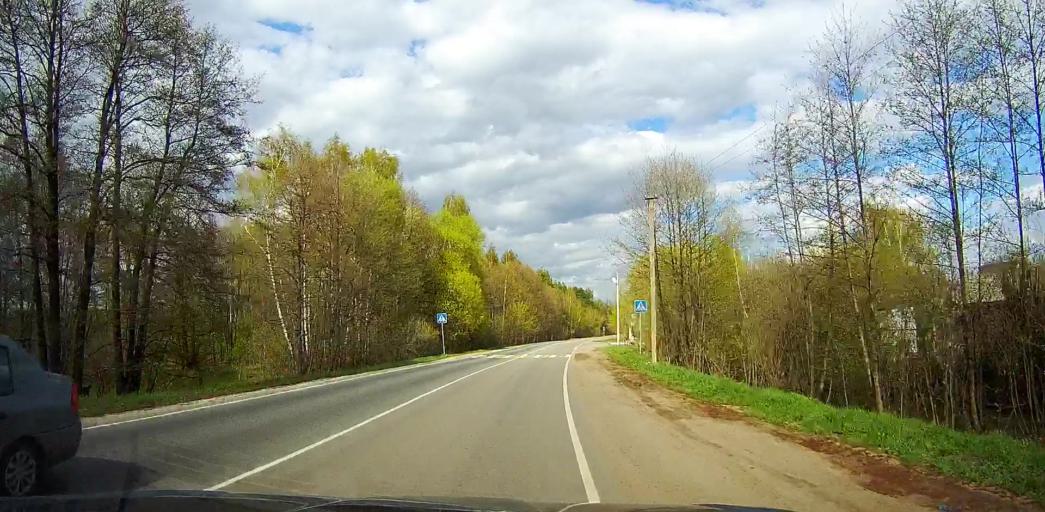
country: RU
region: Moskovskaya
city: Rakhmanovo
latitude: 55.7351
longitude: 38.6343
